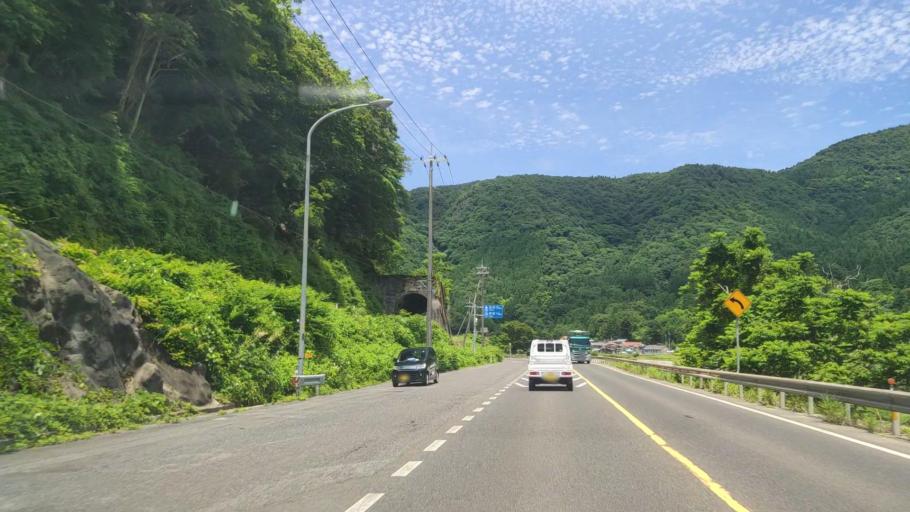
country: JP
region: Tottori
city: Tottori
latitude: 35.3647
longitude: 134.3780
